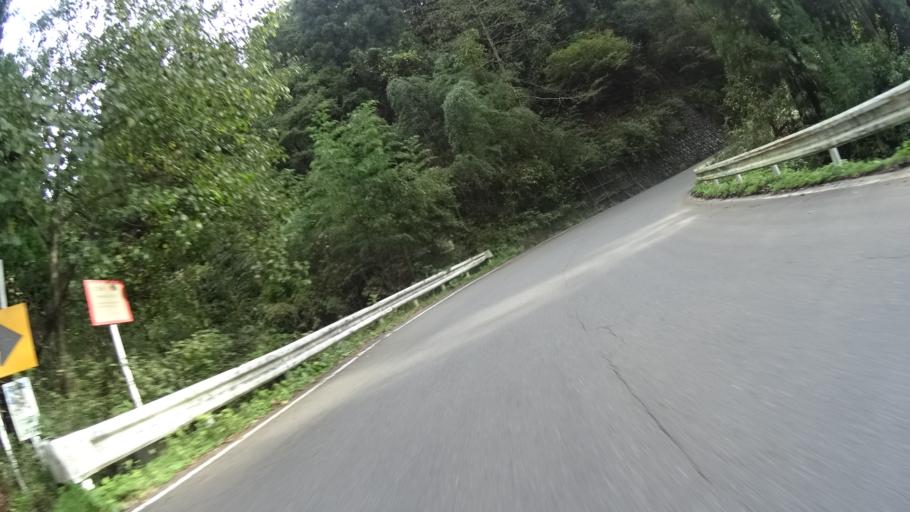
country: JP
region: Yamanashi
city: Uenohara
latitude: 35.6755
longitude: 139.0920
